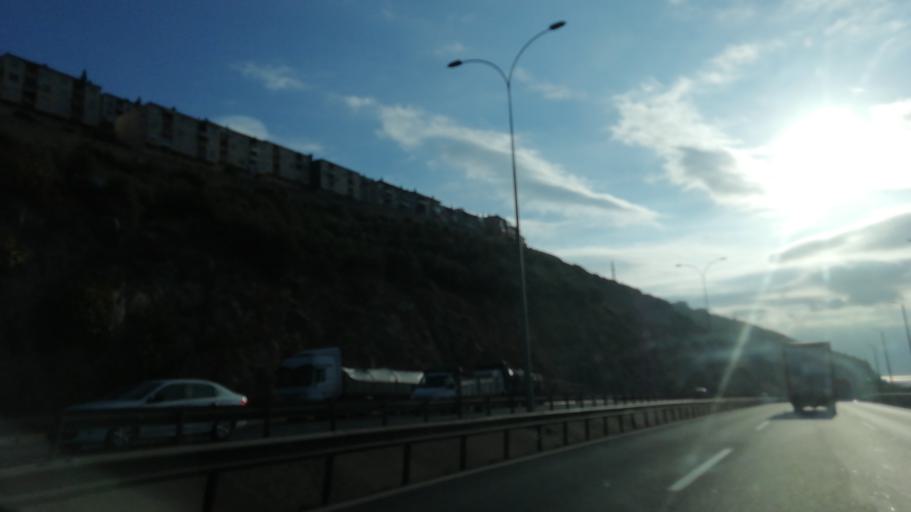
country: TR
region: Kocaeli
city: Hereke
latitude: 40.7854
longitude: 29.6236
